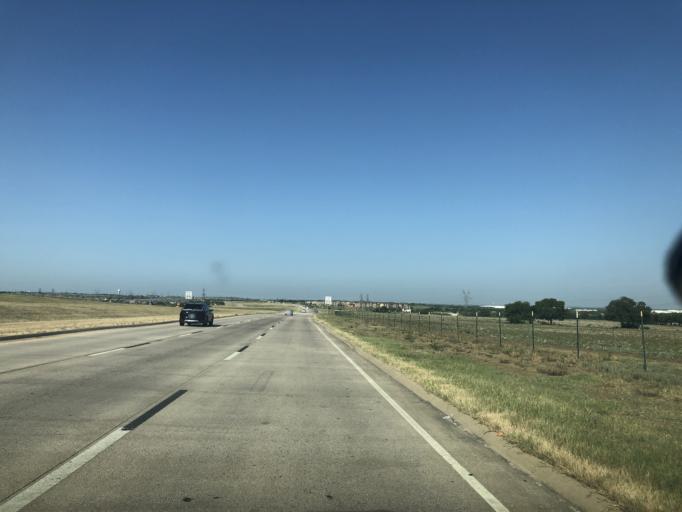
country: US
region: Texas
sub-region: Tarrant County
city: Keller
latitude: 32.9712
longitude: -97.2823
